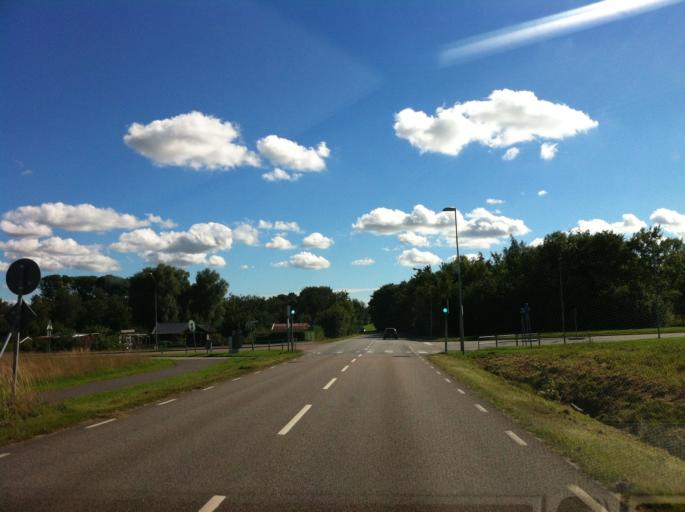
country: SE
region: Skane
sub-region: Svalovs Kommun
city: Kagerod
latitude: 56.0246
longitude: 13.1100
